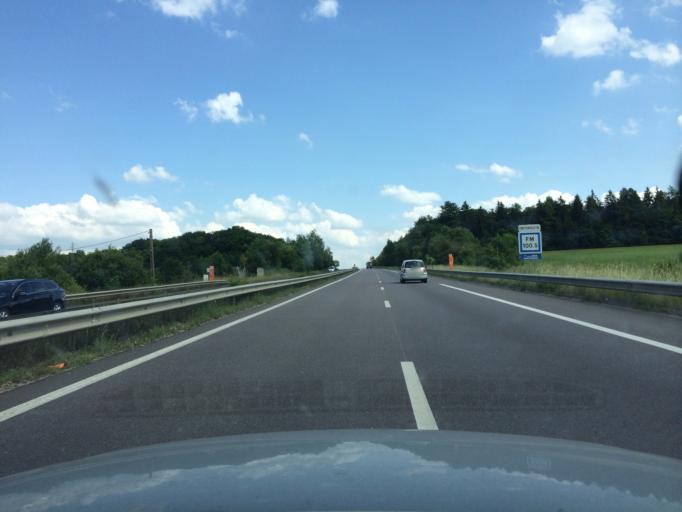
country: FR
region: Lorraine
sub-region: Departement de Meurthe-et-Moselle
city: Foug
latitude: 48.6770
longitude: 5.7591
